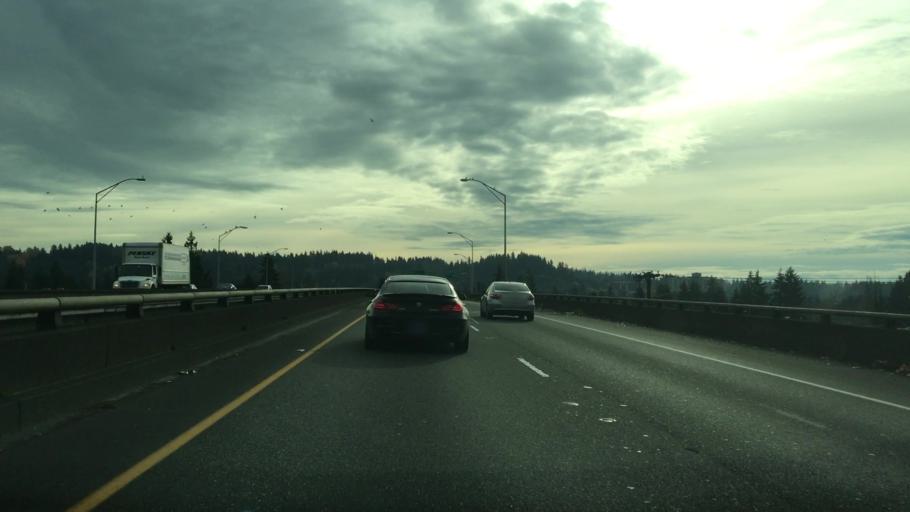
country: US
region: Washington
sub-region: Pierce County
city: Puyallup
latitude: 47.1922
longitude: -122.2828
